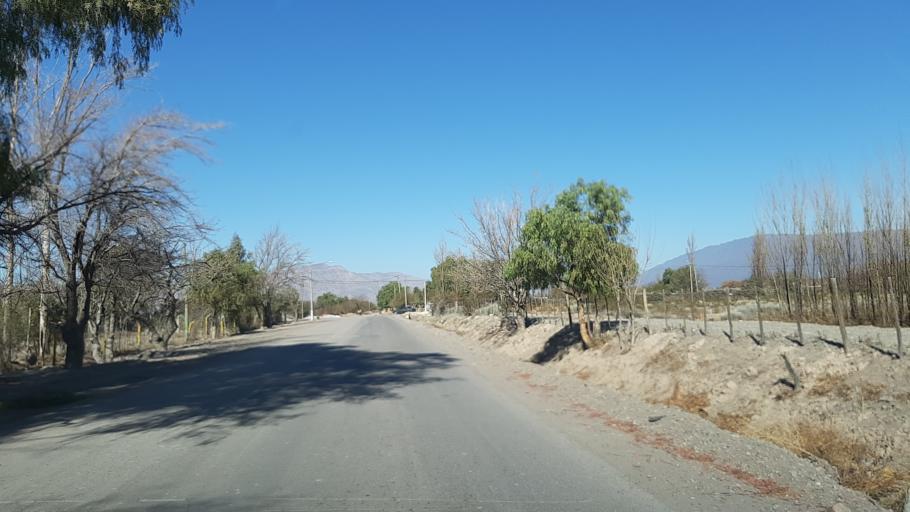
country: AR
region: San Juan
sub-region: Departamento de Zonda
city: Zonda
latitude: -31.4680
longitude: -68.7227
